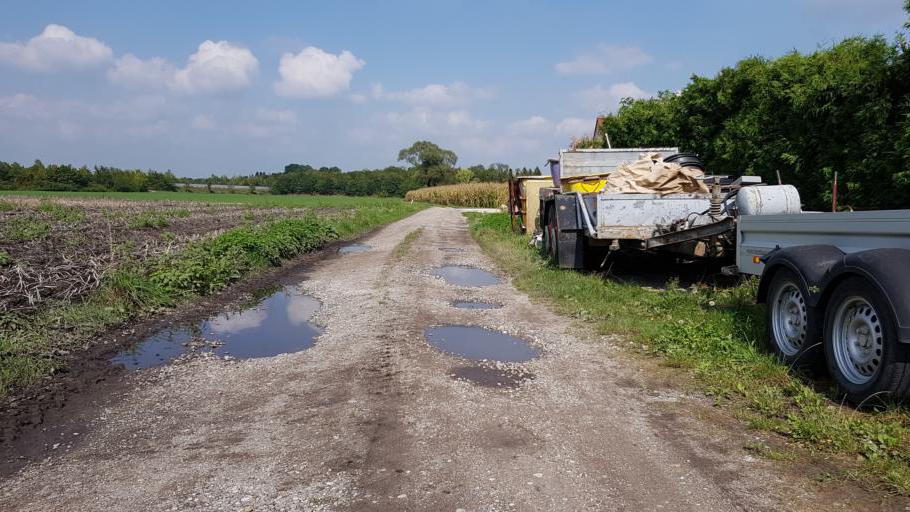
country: DE
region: Bavaria
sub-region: Upper Bavaria
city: Karlsfeld
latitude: 48.2099
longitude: 11.5015
